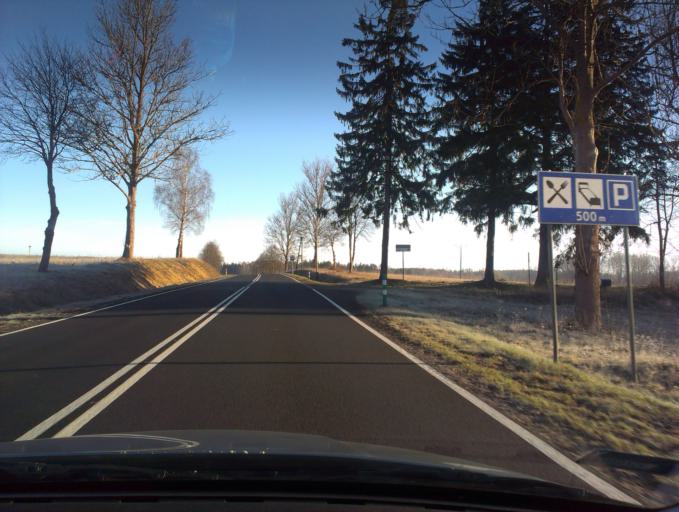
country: PL
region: West Pomeranian Voivodeship
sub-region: Powiat szczecinecki
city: Szczecinek
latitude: 53.8119
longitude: 16.6434
